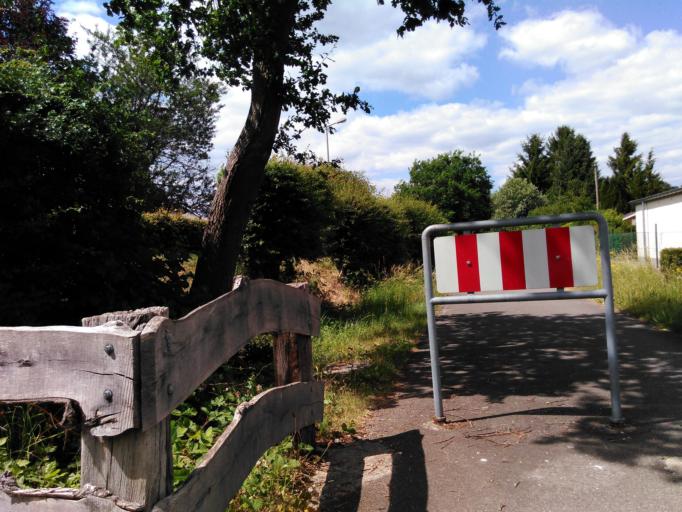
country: LU
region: Luxembourg
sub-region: Canton de Capellen
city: Clemency
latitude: 49.6054
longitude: 5.8779
